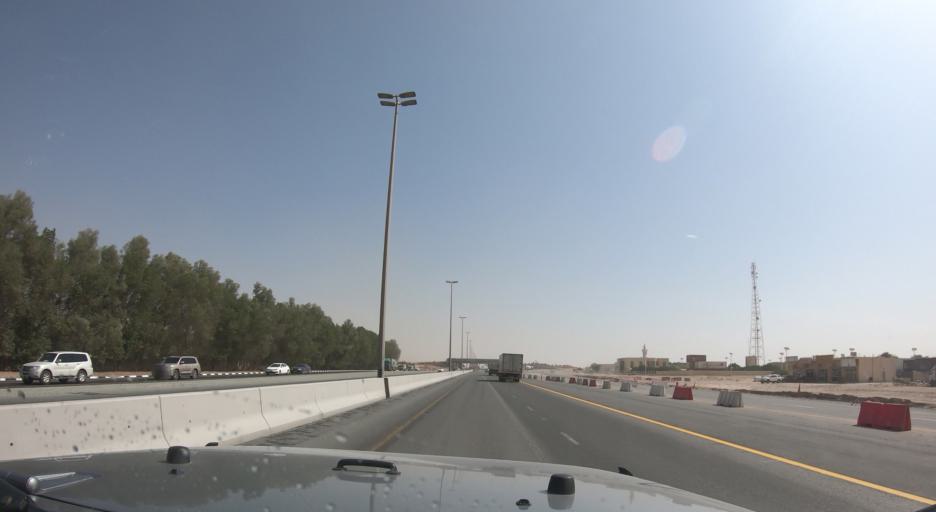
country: AE
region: Ash Shariqah
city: Sharjah
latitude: 25.2932
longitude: 55.6163
